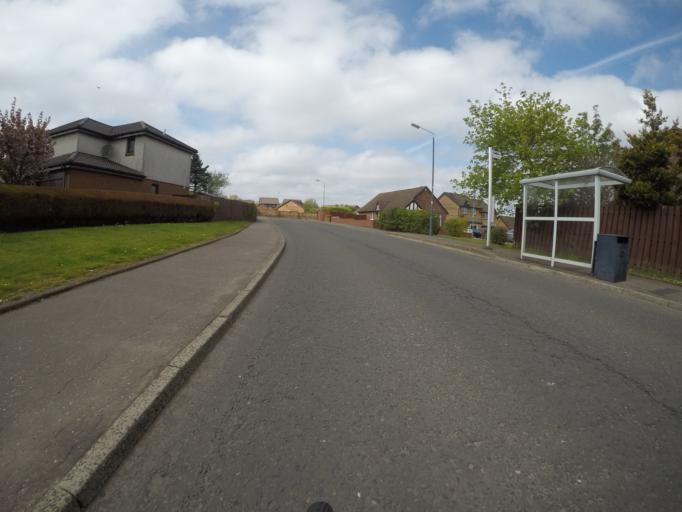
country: GB
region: Scotland
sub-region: East Renfrewshire
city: Newton Mearns
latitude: 55.7794
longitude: -4.3489
